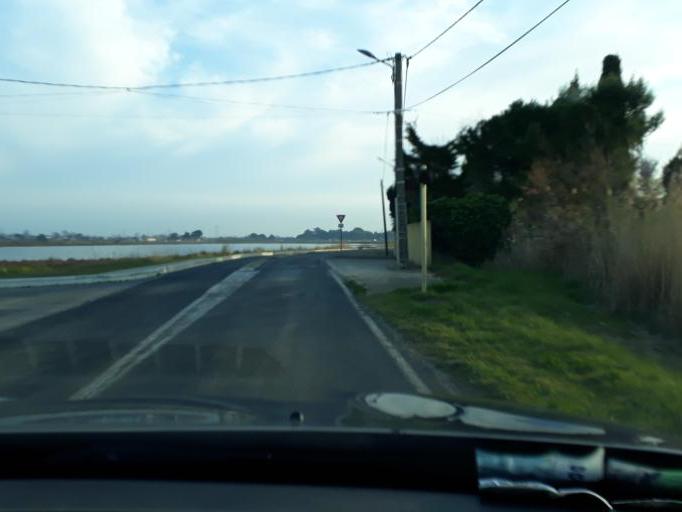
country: FR
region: Languedoc-Roussillon
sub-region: Departement de l'Herault
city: Marseillan
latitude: 43.3295
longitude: 3.5321
